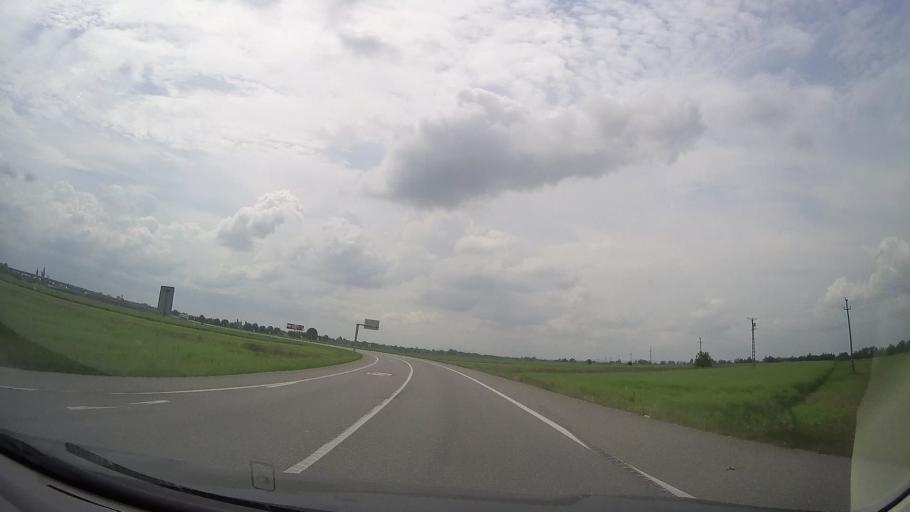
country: RO
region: Timis
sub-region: Comuna Costeiu
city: Costeiu
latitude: 45.7262
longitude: 21.8700
